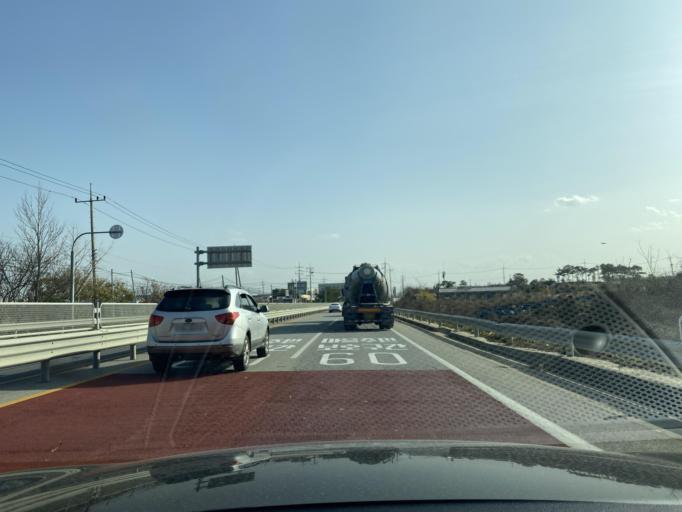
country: KR
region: Chungcheongnam-do
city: Yesan
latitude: 36.6903
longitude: 126.7479
